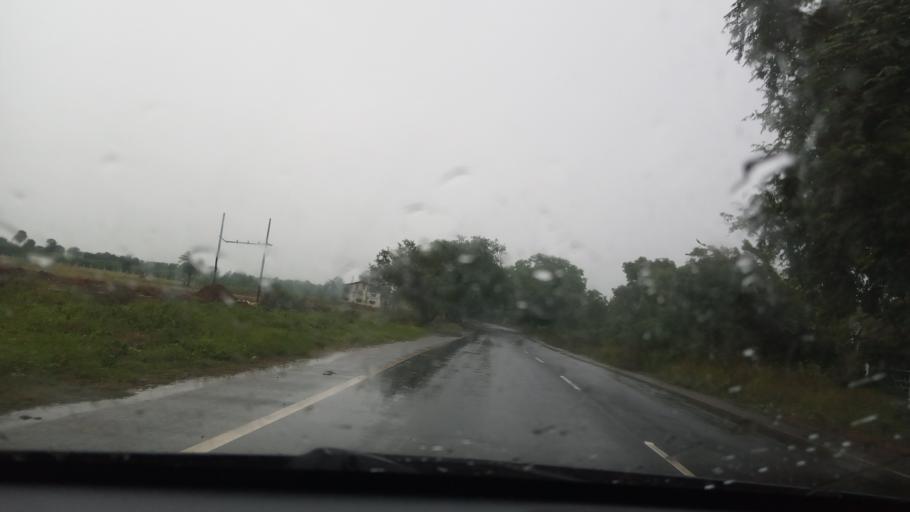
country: IN
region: Tamil Nadu
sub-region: Vellore
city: Kalavai
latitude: 12.8047
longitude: 79.4265
